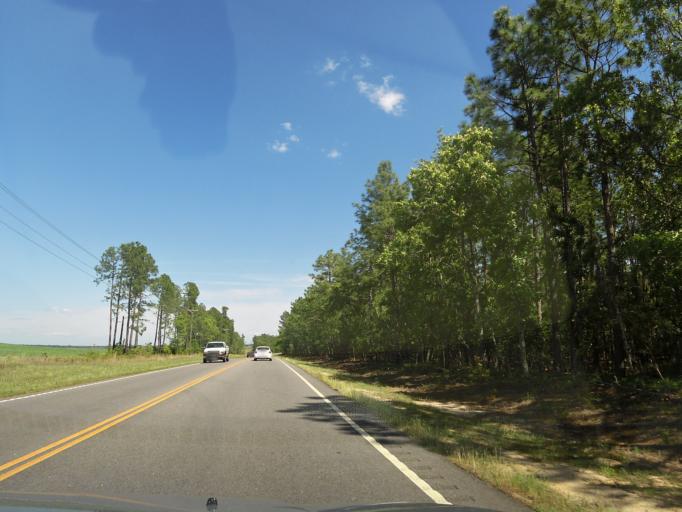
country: US
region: South Carolina
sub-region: Aiken County
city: New Ellenton
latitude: 33.5121
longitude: -81.5658
